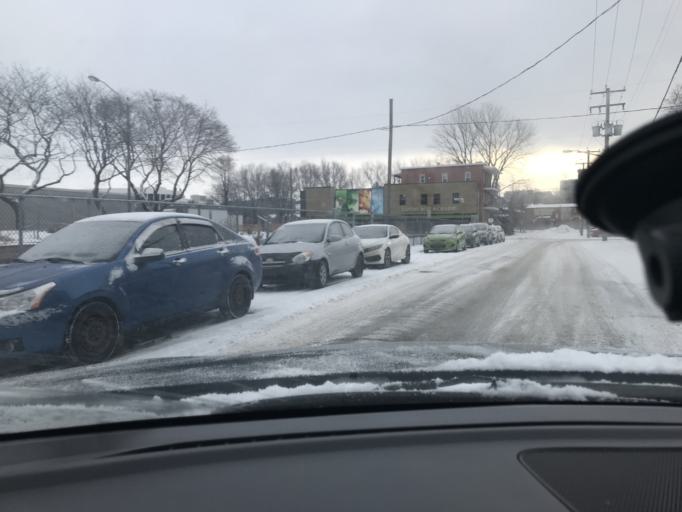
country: CA
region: Quebec
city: Quebec
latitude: 46.8214
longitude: -71.2225
